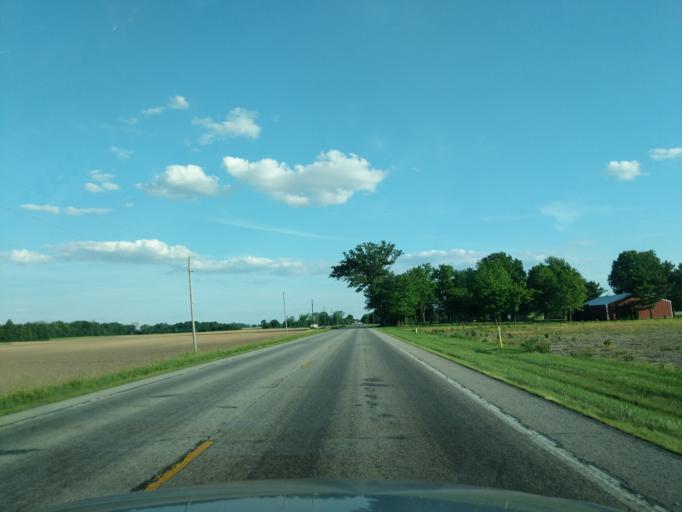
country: US
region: Indiana
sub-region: Huntington County
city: Huntington
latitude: 40.7968
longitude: -85.4599
